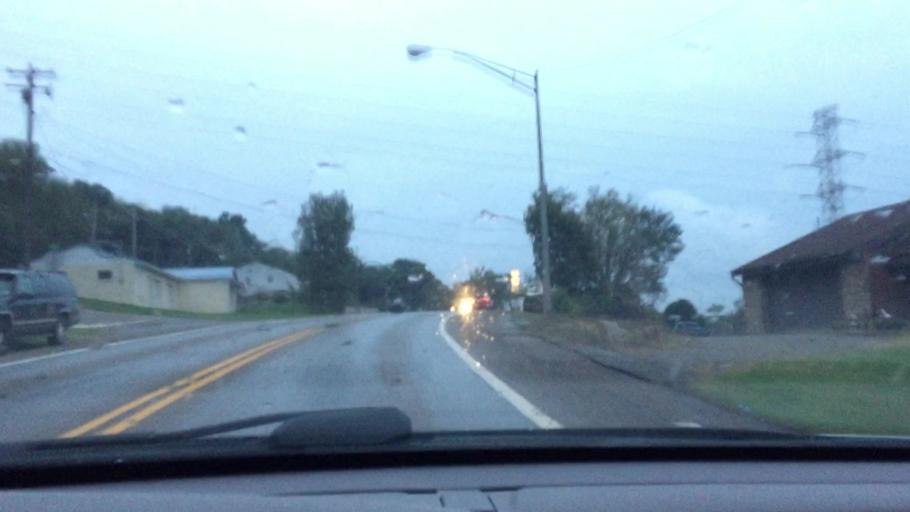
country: US
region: Pennsylvania
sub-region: Allegheny County
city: Cheswick
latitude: 40.5565
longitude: -79.8155
